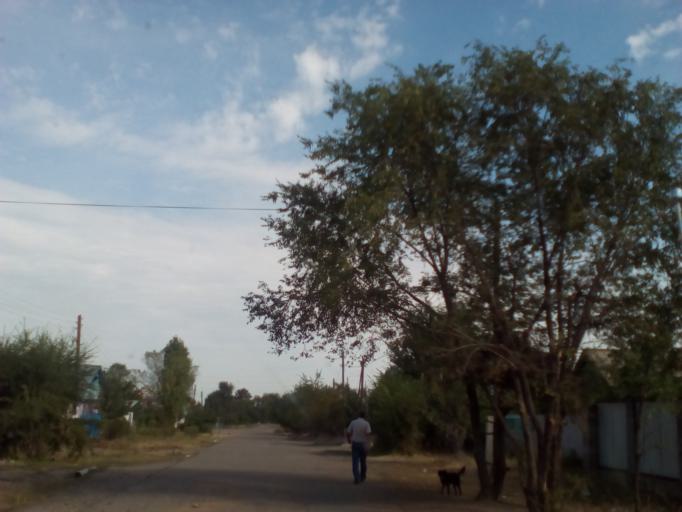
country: KZ
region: Almaty Oblysy
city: Burunday
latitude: 43.1669
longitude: 76.4050
